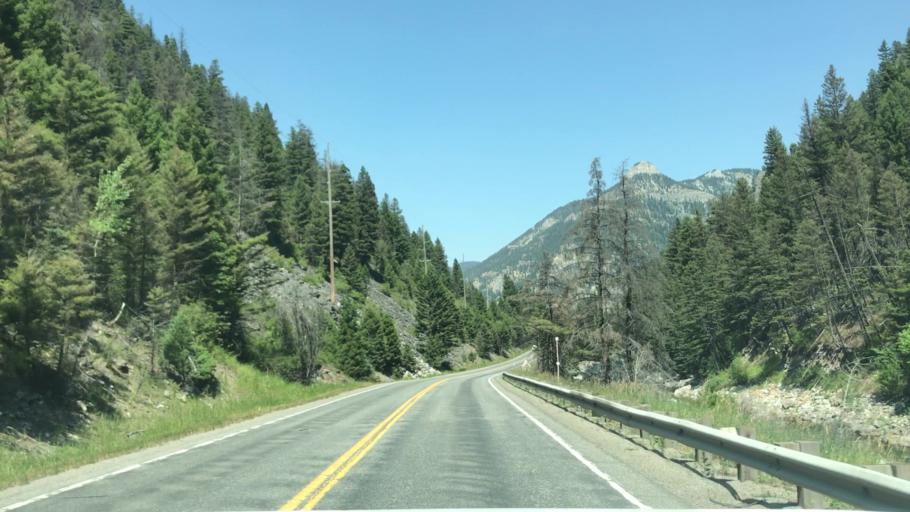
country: US
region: Montana
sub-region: Gallatin County
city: Big Sky
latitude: 45.4231
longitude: -111.2342
